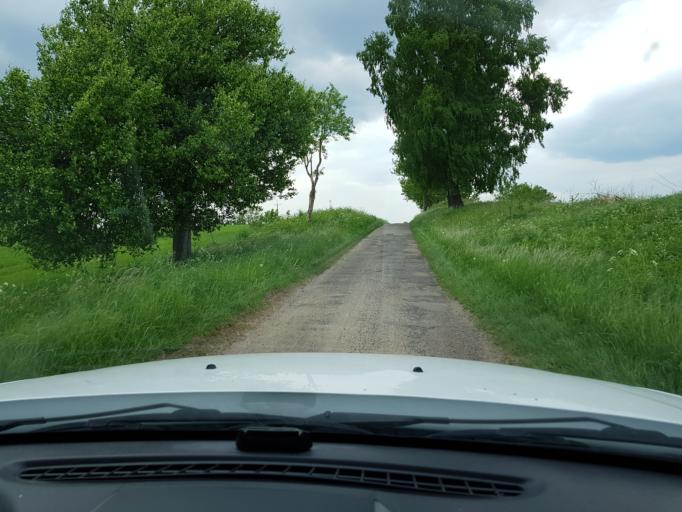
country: PL
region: West Pomeranian Voivodeship
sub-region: Powiat drawski
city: Drawsko Pomorskie
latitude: 53.5222
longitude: 15.7502
